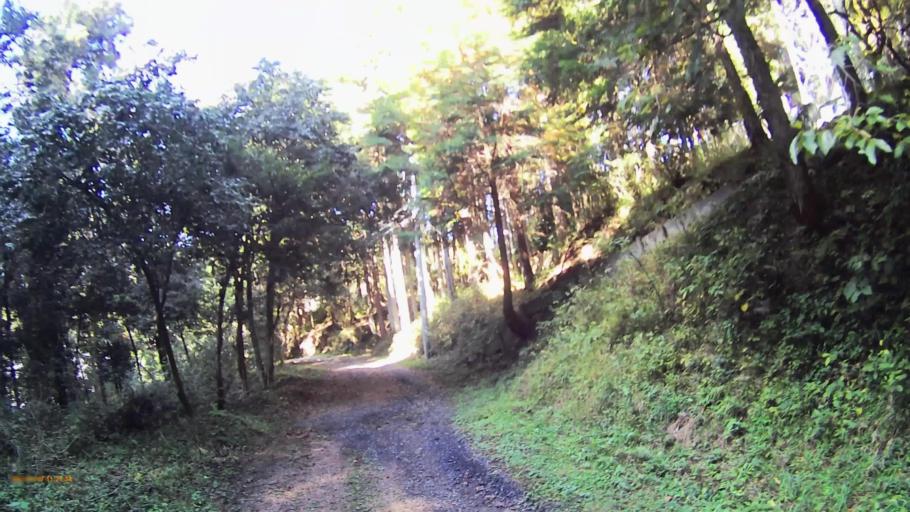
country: JP
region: Gifu
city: Mizunami
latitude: 35.4337
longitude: 137.2977
